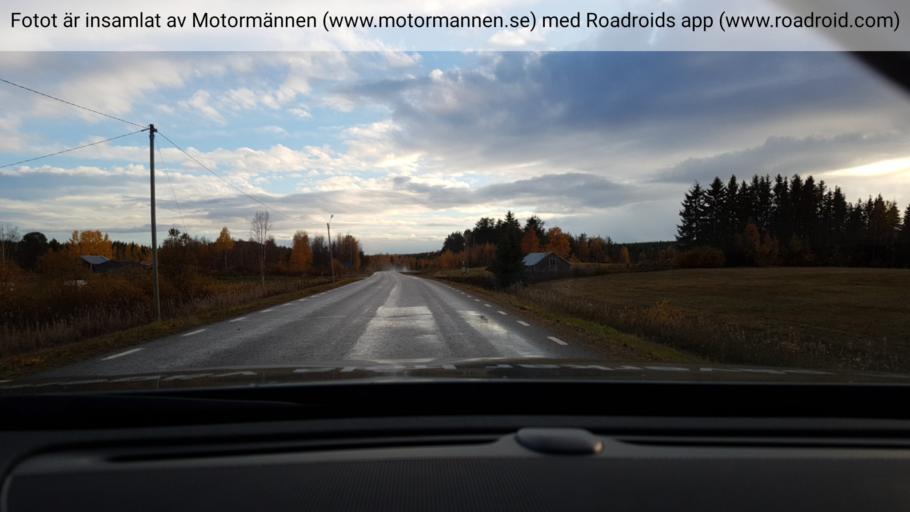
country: SE
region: Norrbotten
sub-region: Overkalix Kommun
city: OEverkalix
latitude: 66.7652
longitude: 22.6834
